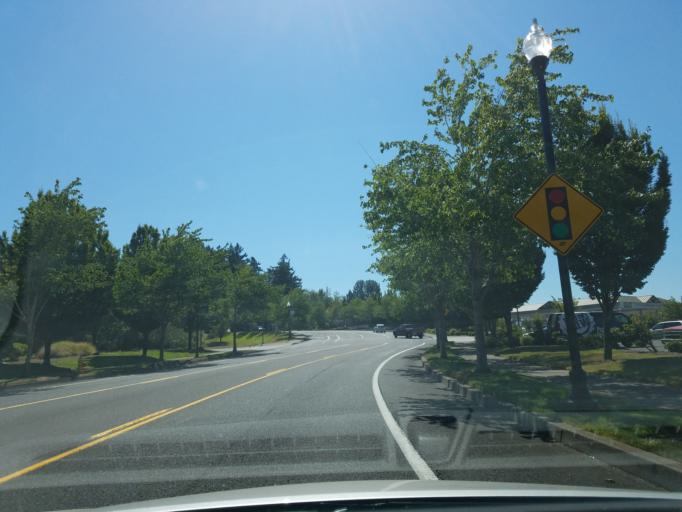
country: US
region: Oregon
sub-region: Multnomah County
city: Wood Village
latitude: 45.5295
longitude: -122.4274
